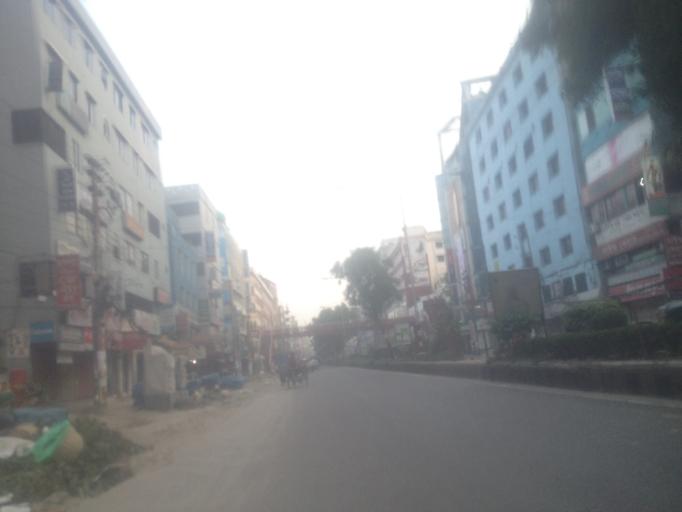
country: BD
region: Dhaka
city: Azimpur
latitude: 23.7905
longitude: 90.3756
